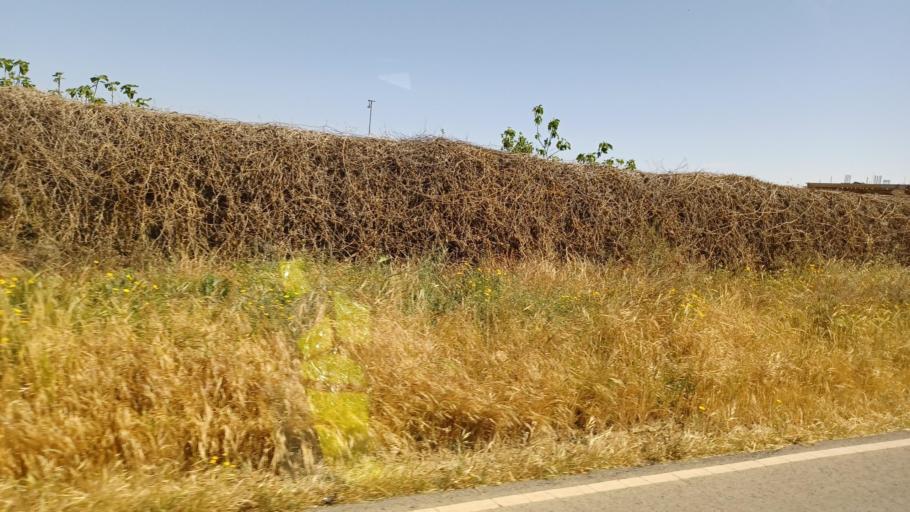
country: CY
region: Lefkosia
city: Kokkinotrimithia
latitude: 35.1583
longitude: 33.1778
